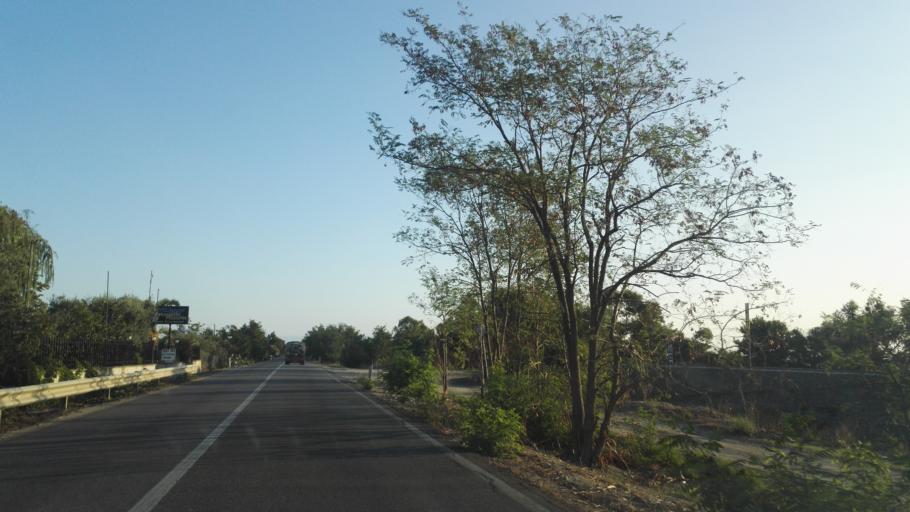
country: IT
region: Calabria
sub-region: Provincia di Catanzaro
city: Santa Caterina dello Ionio Marina
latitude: 38.5504
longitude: 16.5703
